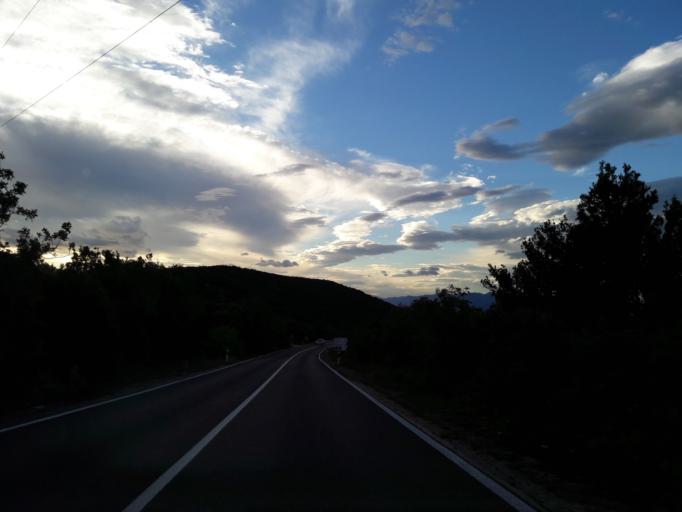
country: BA
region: Federation of Bosnia and Herzegovina
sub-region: Hercegovacko-Bosanski Kanton
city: Neum
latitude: 42.9067
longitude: 17.4793
